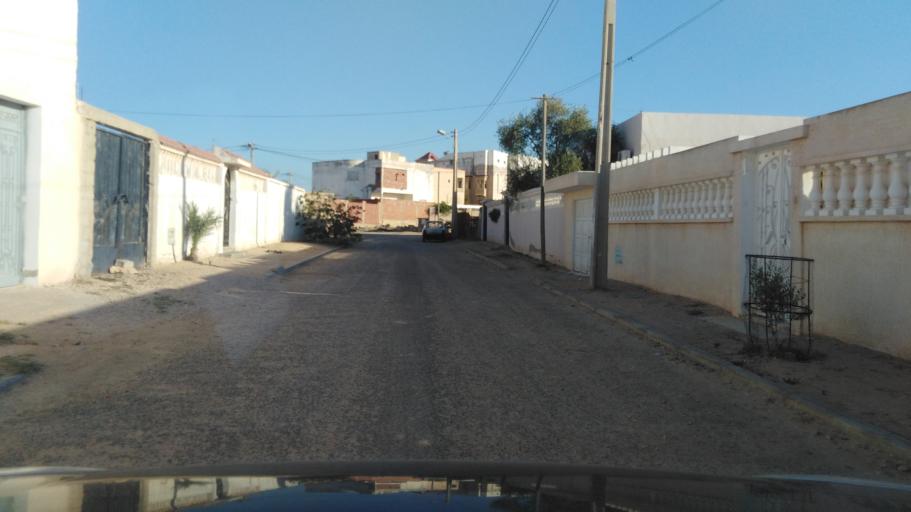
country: TN
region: Qabis
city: Gabes
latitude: 33.9522
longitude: 10.0112
